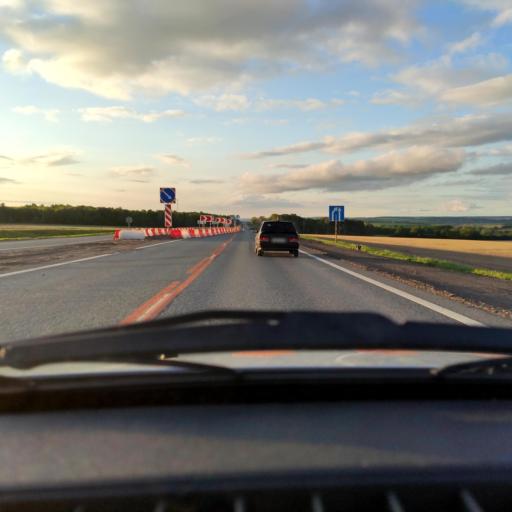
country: RU
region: Bashkortostan
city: Tolbazy
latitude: 54.1080
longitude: 55.8998
